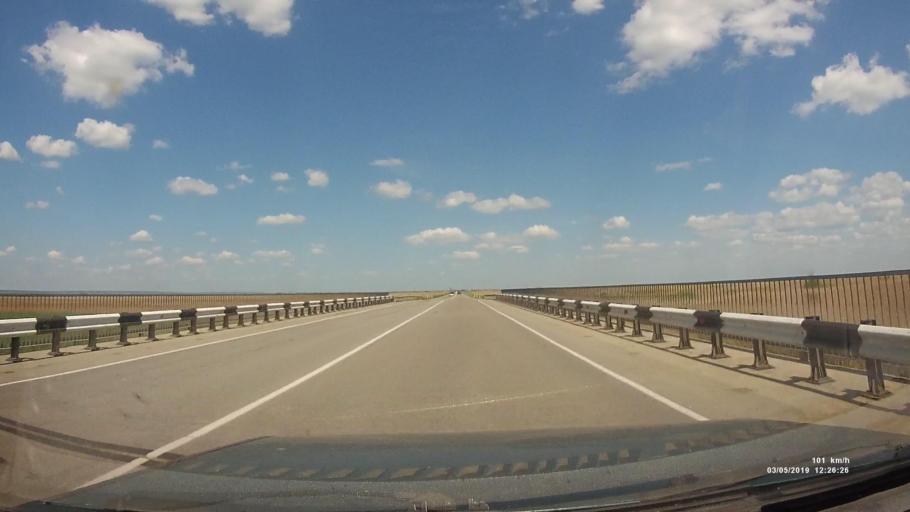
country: RU
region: Rostov
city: Semikarakorsk
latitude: 47.4453
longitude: 40.7137
